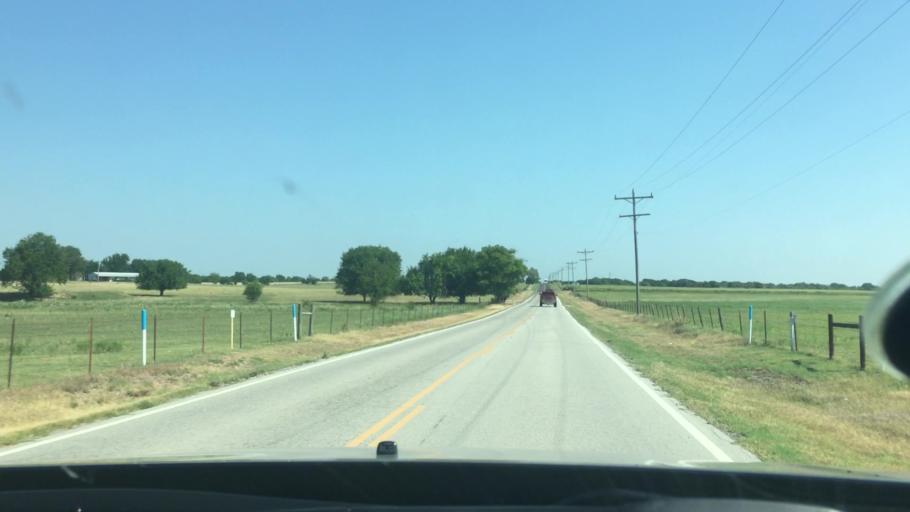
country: US
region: Oklahoma
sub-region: Bryan County
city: Durant
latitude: 34.1109
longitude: -96.4877
